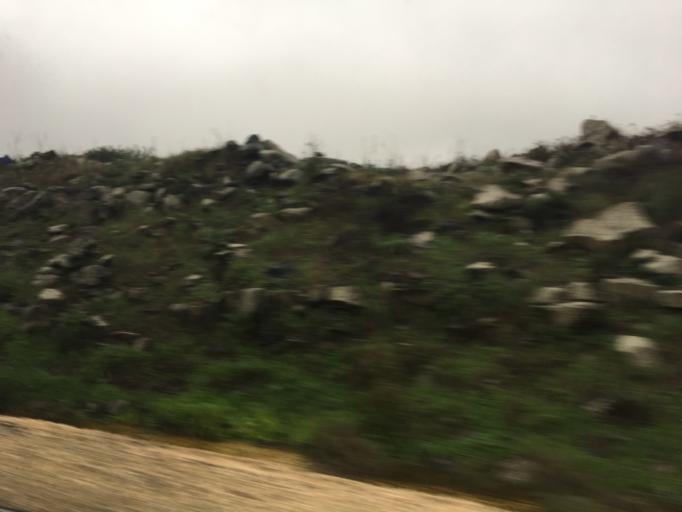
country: SY
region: Quneitra
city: Al Khushniyah
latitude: 32.9766
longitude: 35.7510
